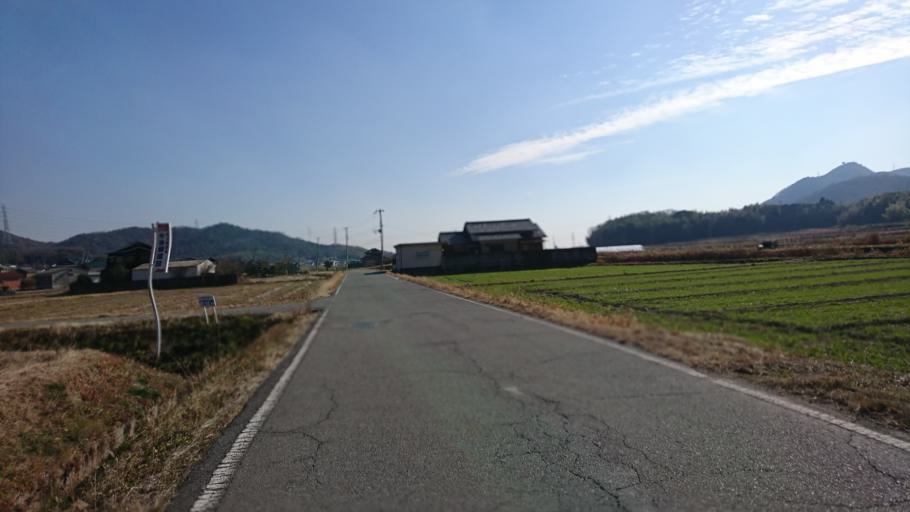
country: JP
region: Hyogo
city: Kakogawacho-honmachi
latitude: 34.8224
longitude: 134.8453
